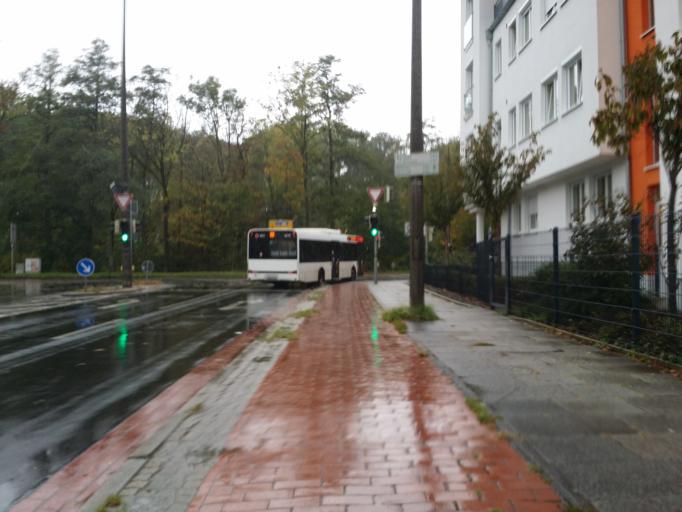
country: DE
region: Bremen
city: Bremen
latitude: 53.0397
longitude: 8.8149
